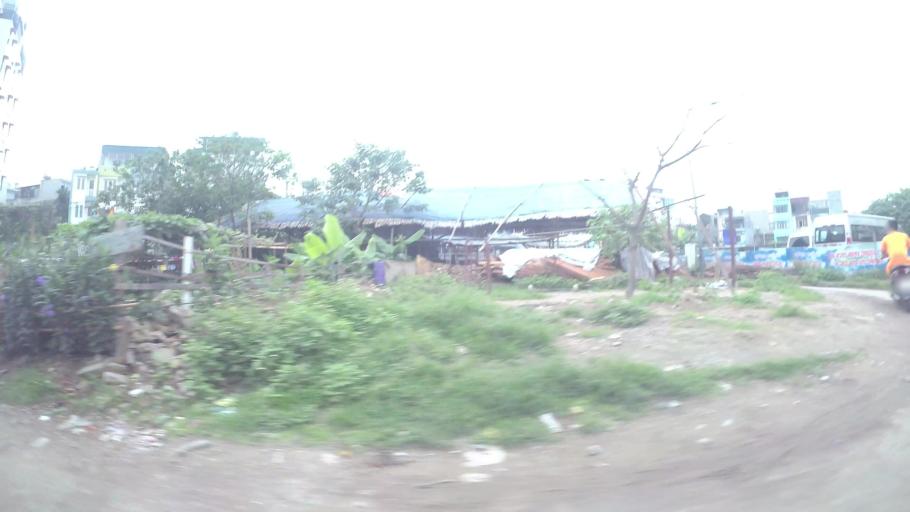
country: VN
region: Ha Noi
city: Hai BaTrung
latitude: 20.9979
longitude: 105.8831
